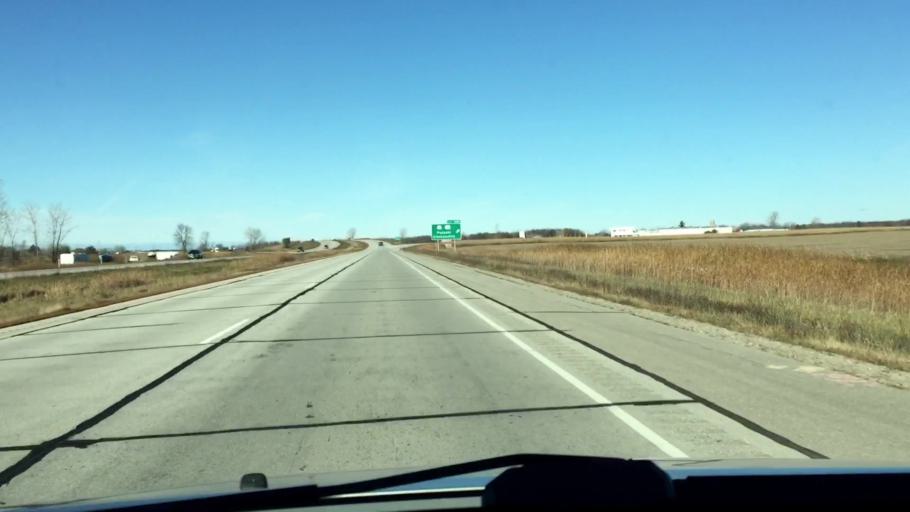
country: US
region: Wisconsin
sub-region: Brown County
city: Pulaski
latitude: 44.5940
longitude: -88.2117
